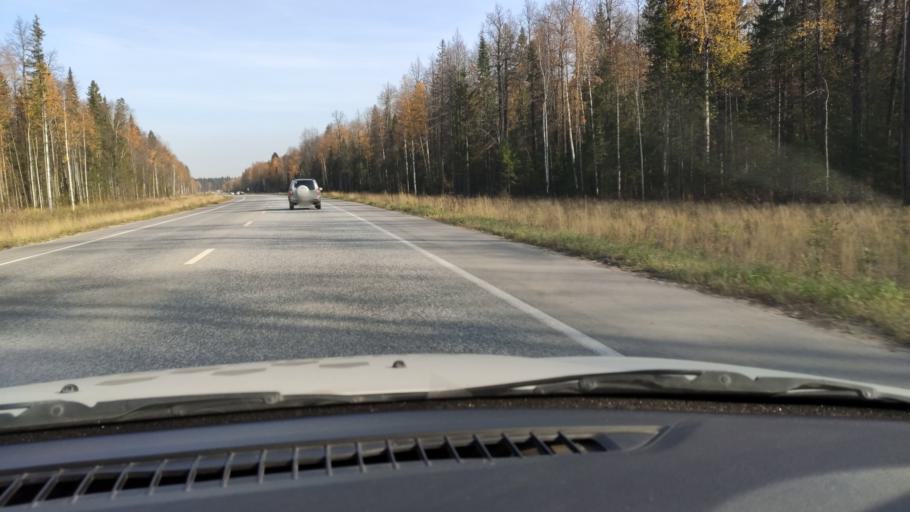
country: RU
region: Perm
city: Novyye Lyady
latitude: 58.0355
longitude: 56.5339
